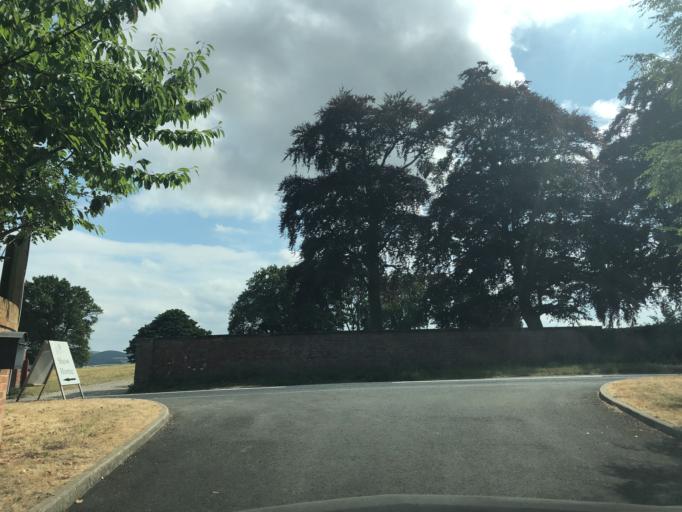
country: GB
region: England
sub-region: North Yorkshire
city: Stokesley
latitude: 54.4580
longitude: -1.2659
